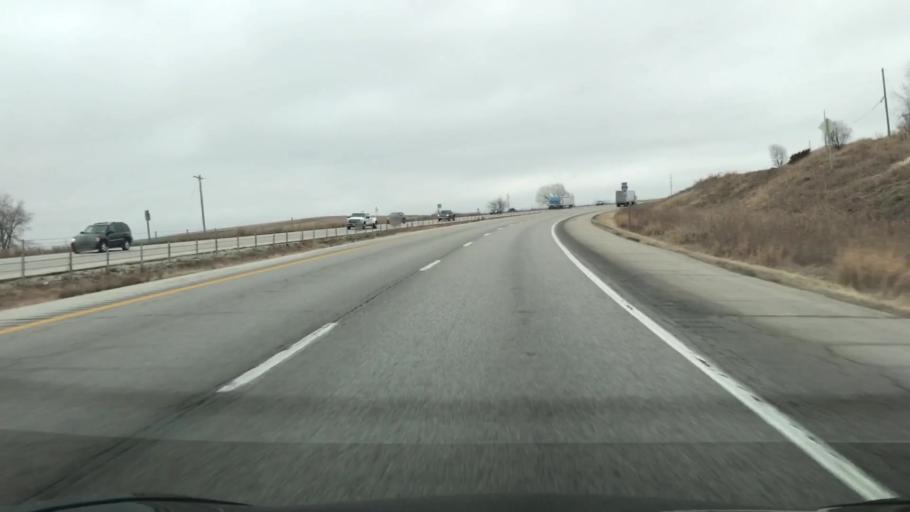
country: US
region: Iowa
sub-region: Madison County
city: Earlham
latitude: 41.5169
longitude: -94.1911
